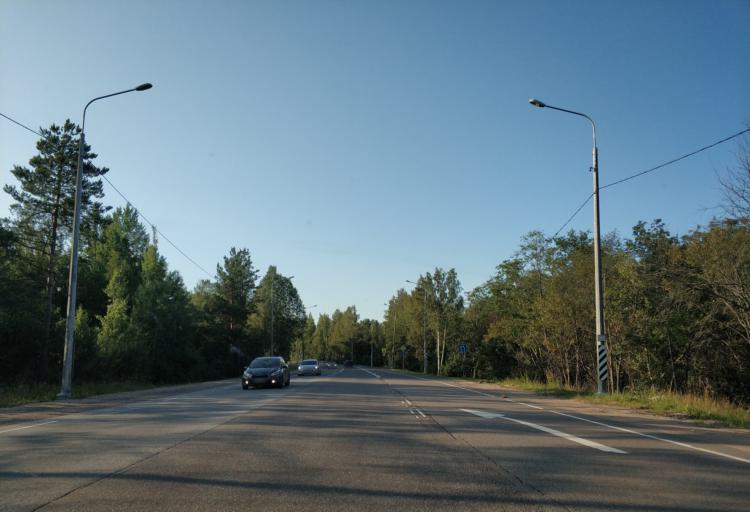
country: RU
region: Leningrad
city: Sapernoye
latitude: 60.6994
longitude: 29.9723
